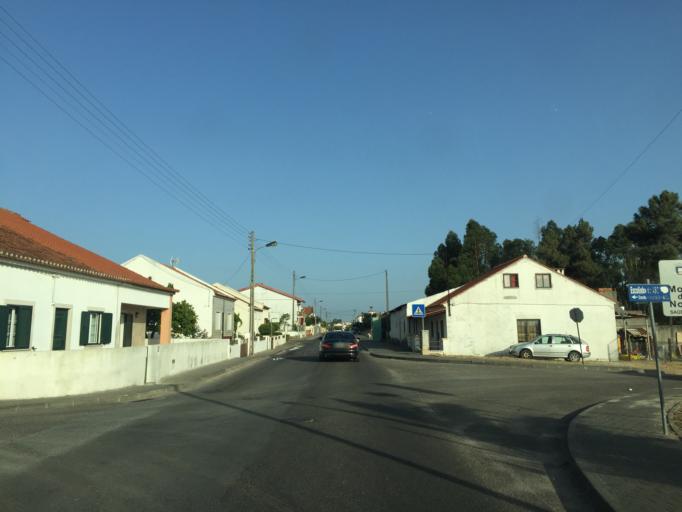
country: PT
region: Santarem
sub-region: Entroncamento
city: Entroncamento
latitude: 39.4727
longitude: -8.4460
